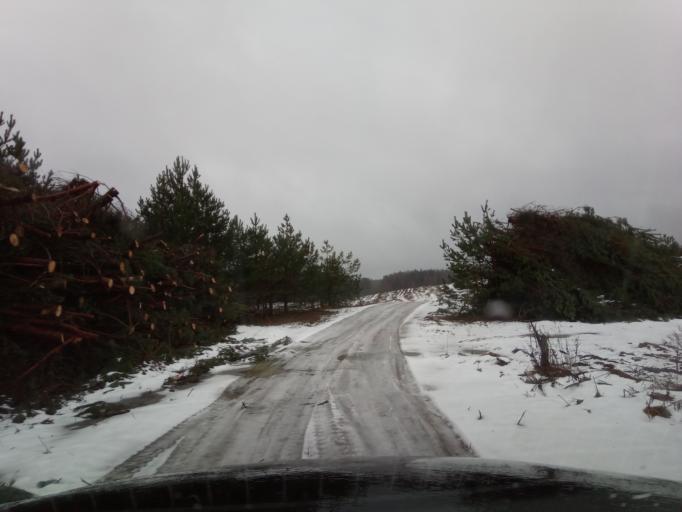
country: LT
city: Svencioneliai
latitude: 55.3412
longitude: 25.8450
